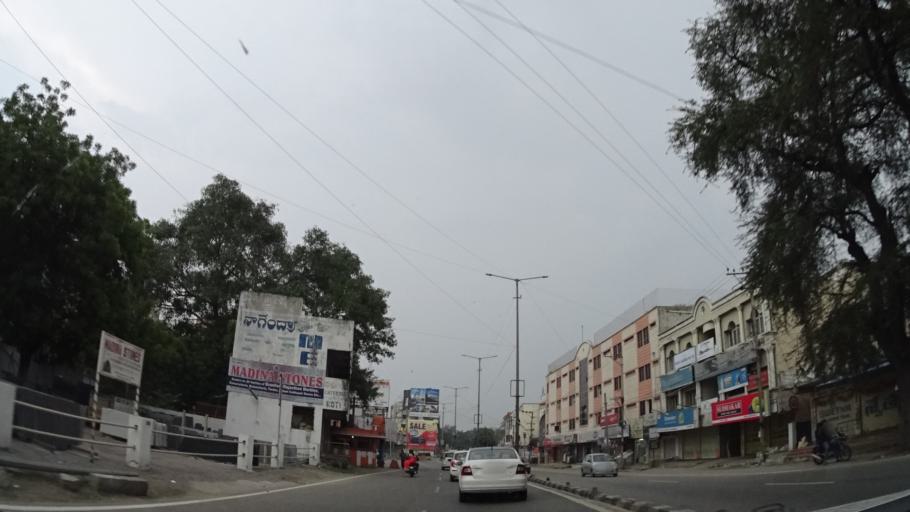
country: IN
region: Telangana
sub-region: Rangareddi
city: Quthbullapur
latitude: 17.4596
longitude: 78.4760
